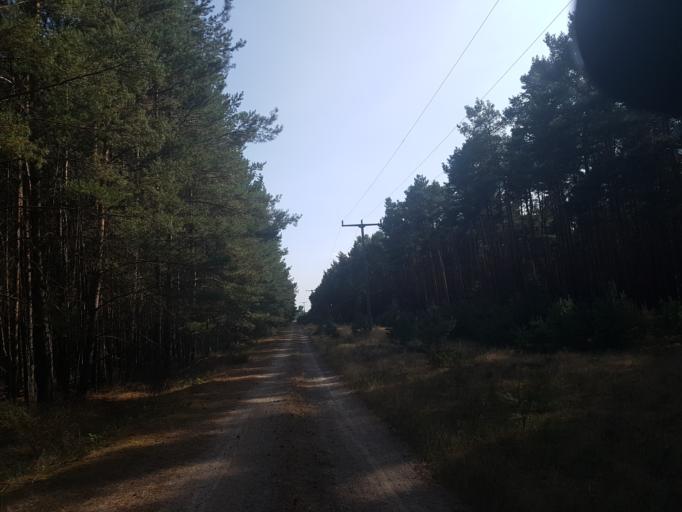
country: DE
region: Saxony-Anhalt
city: Jessen
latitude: 51.8630
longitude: 13.0329
